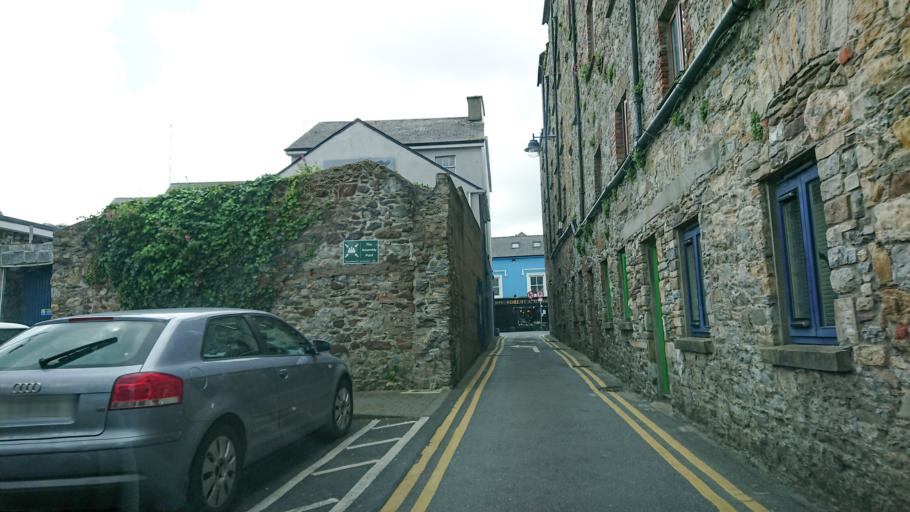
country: IE
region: Munster
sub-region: Waterford
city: Dungarvan
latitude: 52.0893
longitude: -7.6172
